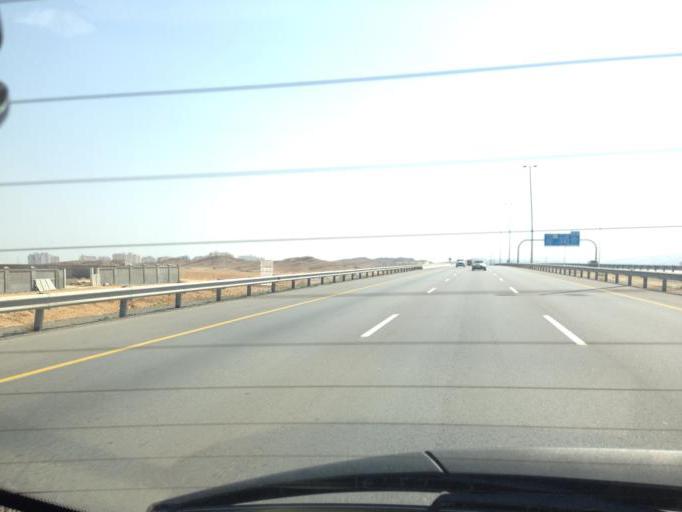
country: OM
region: Muhafazat Masqat
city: As Sib al Jadidah
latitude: 23.5701
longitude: 58.1675
